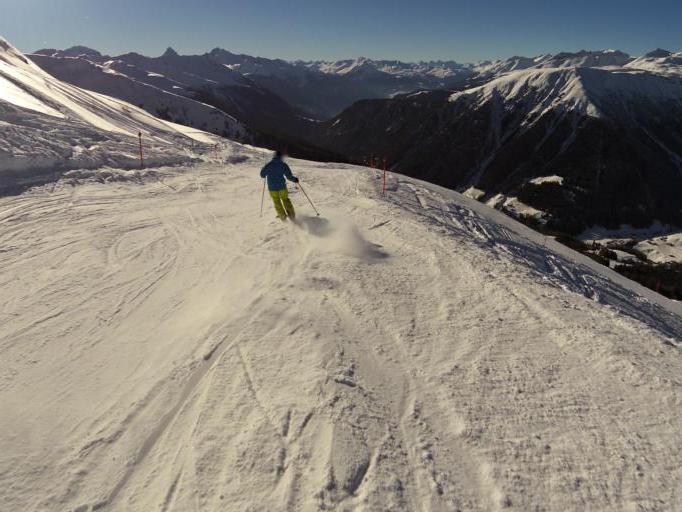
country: CH
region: Grisons
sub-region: Praettigau/Davos District
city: Davos
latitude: 46.7422
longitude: 9.8117
